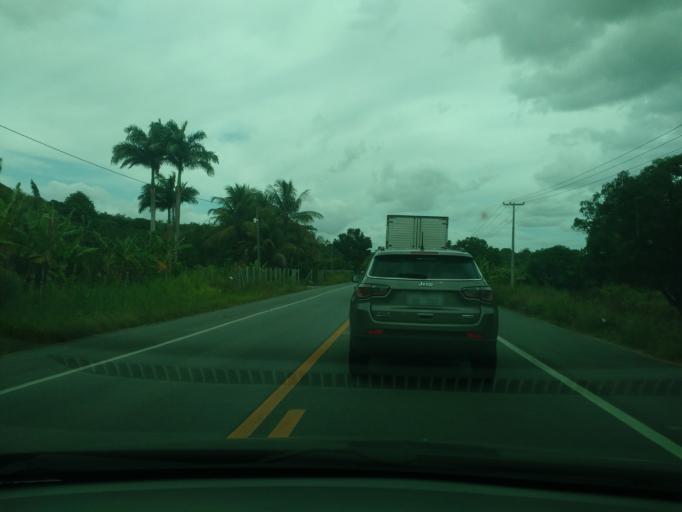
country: BR
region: Alagoas
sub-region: Uniao Dos Palmares
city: Uniao dos Palmares
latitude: -9.2323
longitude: -36.0243
